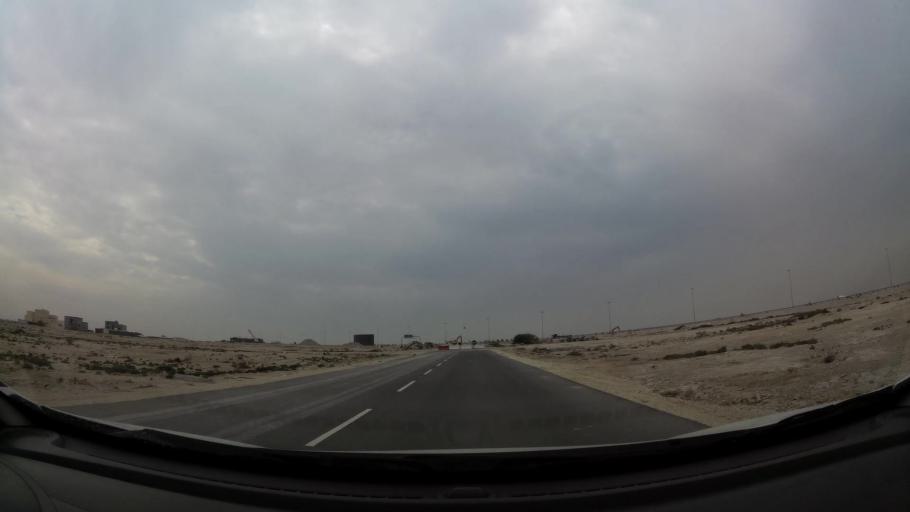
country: BH
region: Northern
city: Ar Rifa'
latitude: 26.0607
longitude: 50.6119
